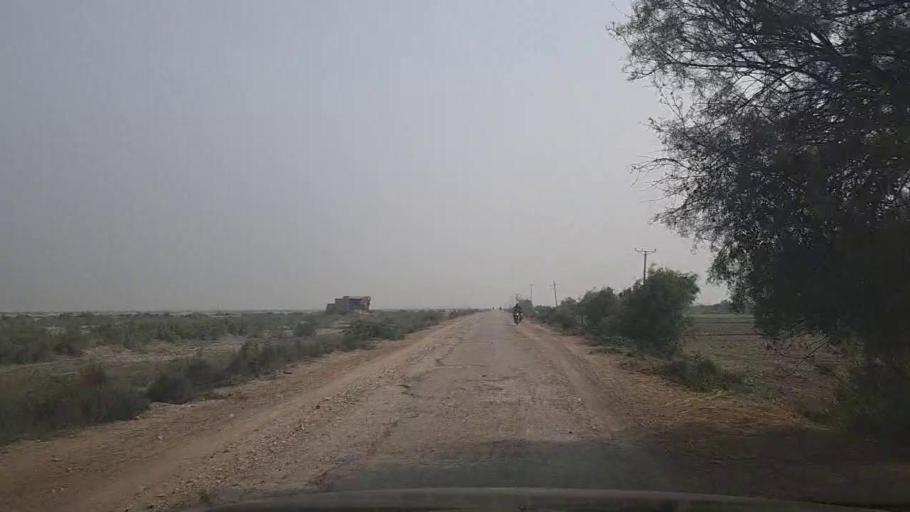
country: PK
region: Sindh
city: Mirpur Sakro
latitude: 24.4697
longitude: 67.6767
